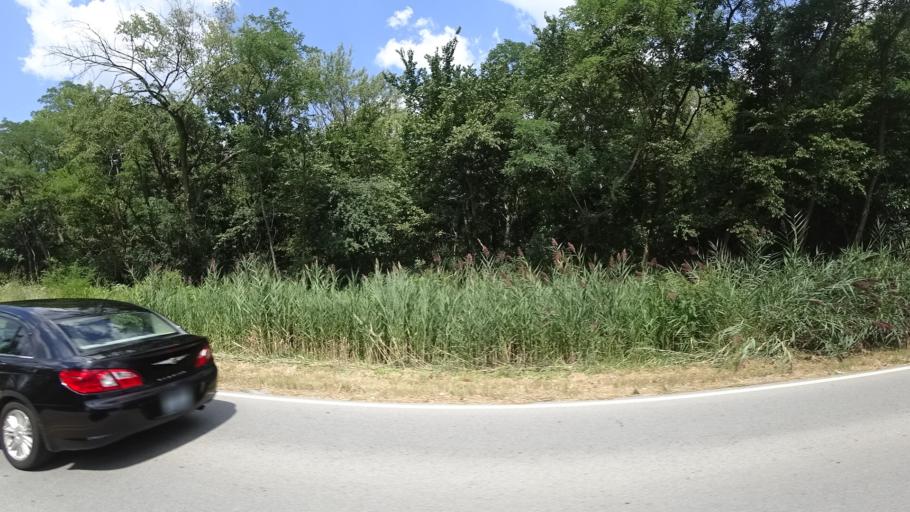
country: US
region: Illinois
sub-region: Cook County
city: Oak Forest
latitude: 41.6245
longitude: -87.7737
